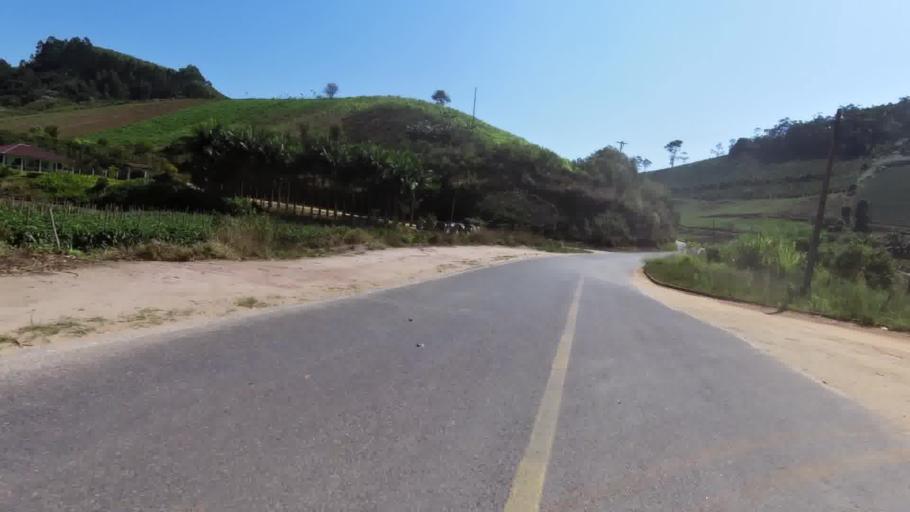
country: BR
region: Espirito Santo
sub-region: Marechal Floriano
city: Marechal Floriano
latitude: -20.4271
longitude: -40.8742
